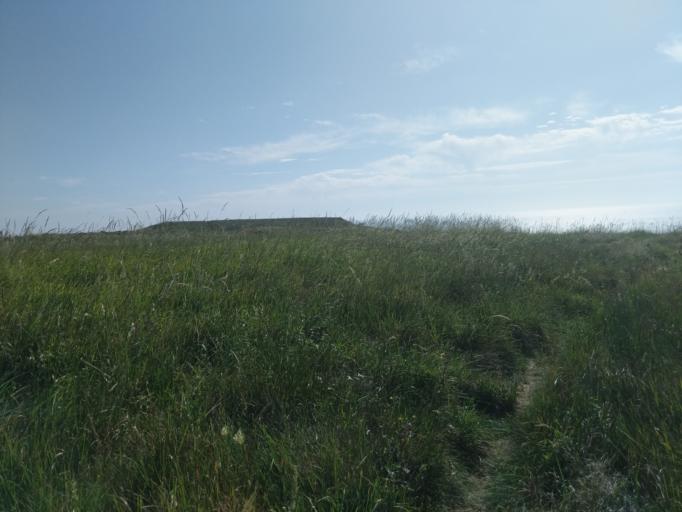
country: GB
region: England
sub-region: Kent
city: Dover
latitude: 51.1019
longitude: 1.2482
